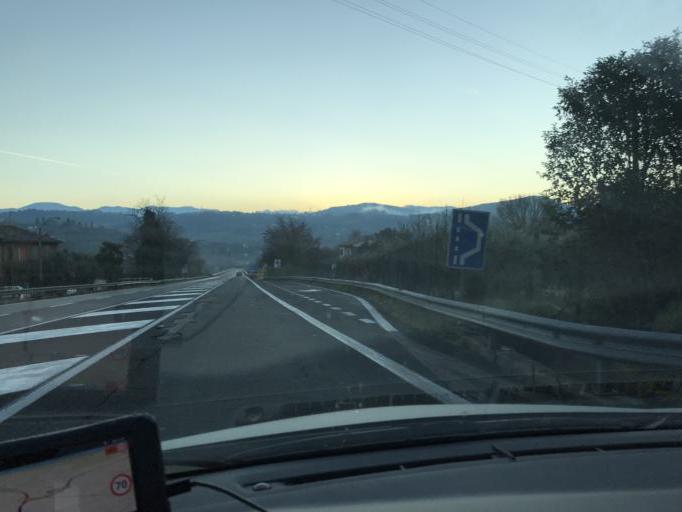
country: IT
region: Umbria
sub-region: Provincia di Terni
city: Terni
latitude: 42.5852
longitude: 12.6696
